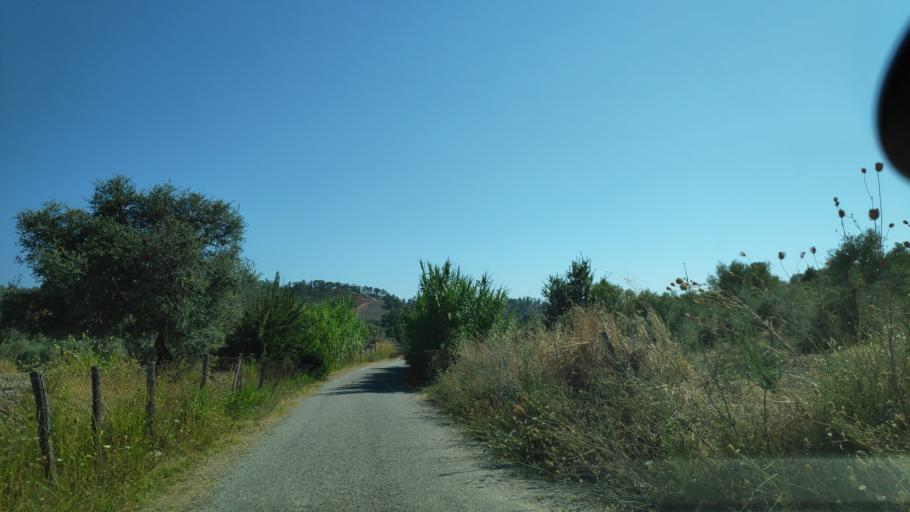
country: IT
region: Calabria
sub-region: Provincia di Reggio Calabria
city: Monasterace
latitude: 38.4312
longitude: 16.5249
